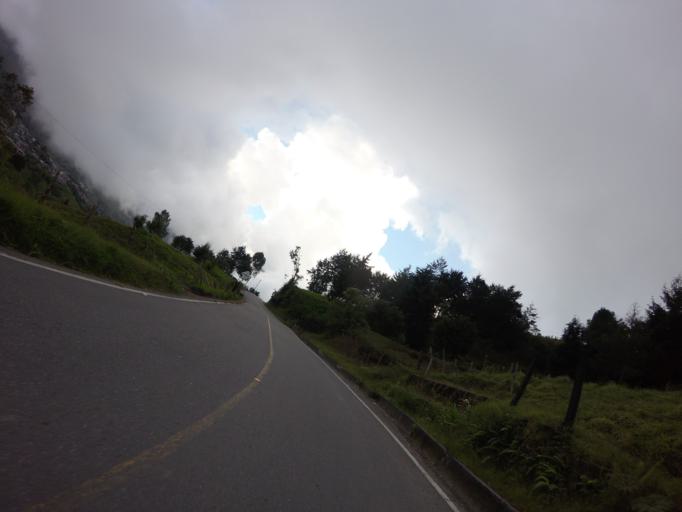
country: CO
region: Caldas
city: Pensilvania
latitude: 5.3775
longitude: -75.1598
